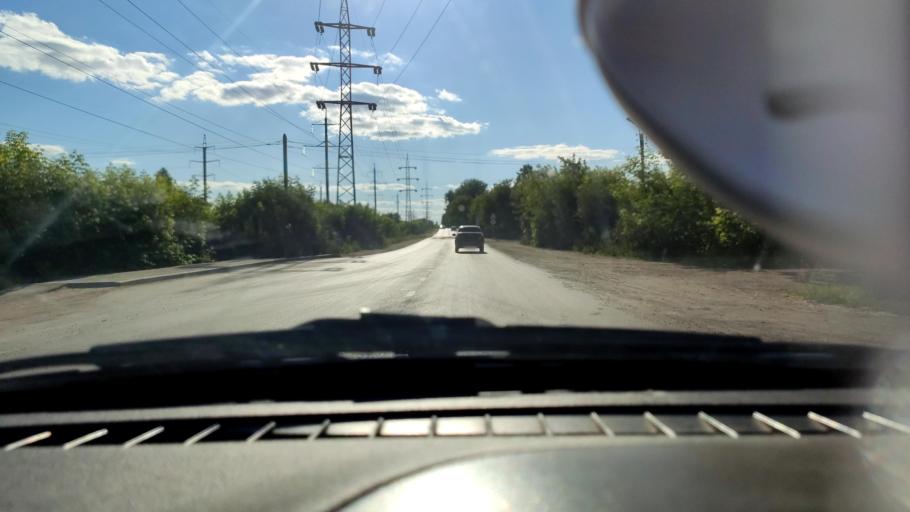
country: RU
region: Perm
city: Krasnokamsk
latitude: 58.0745
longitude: 55.7939
